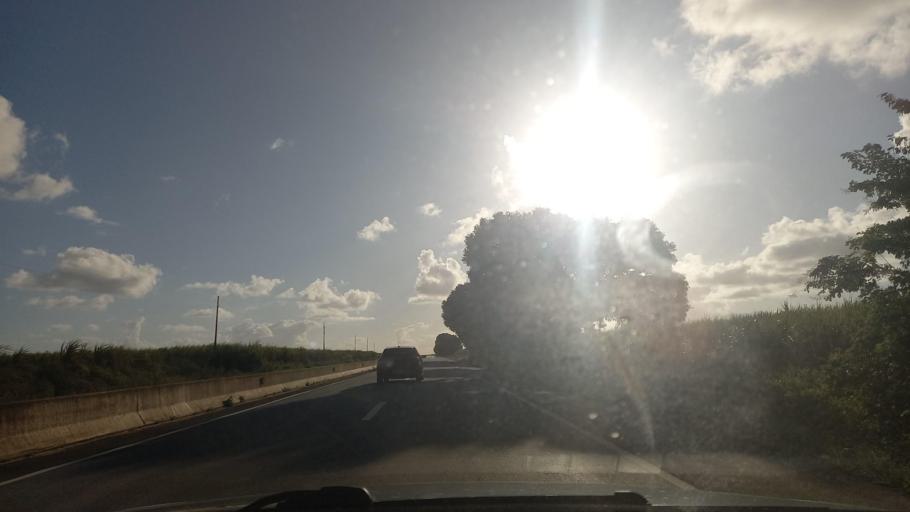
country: BR
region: Alagoas
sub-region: Sao Miguel Dos Campos
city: Sao Miguel dos Campos
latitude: -9.8012
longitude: -36.1549
